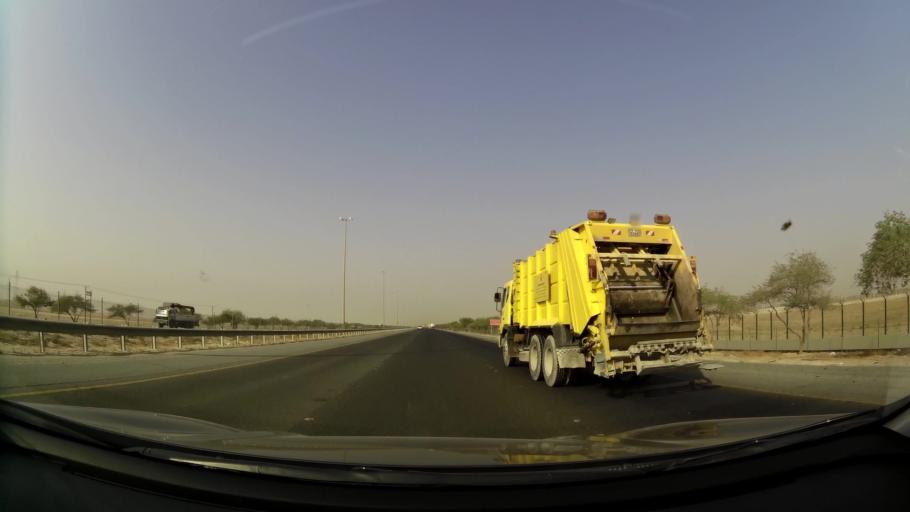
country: KW
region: Al Farwaniyah
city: Janub as Surrah
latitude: 29.1830
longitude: 47.9610
